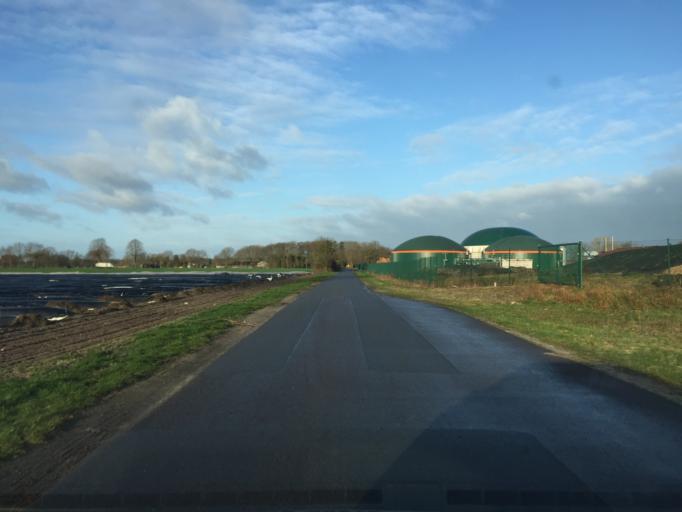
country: DE
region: Lower Saxony
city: Steyerberg
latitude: 52.5926
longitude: 8.9863
